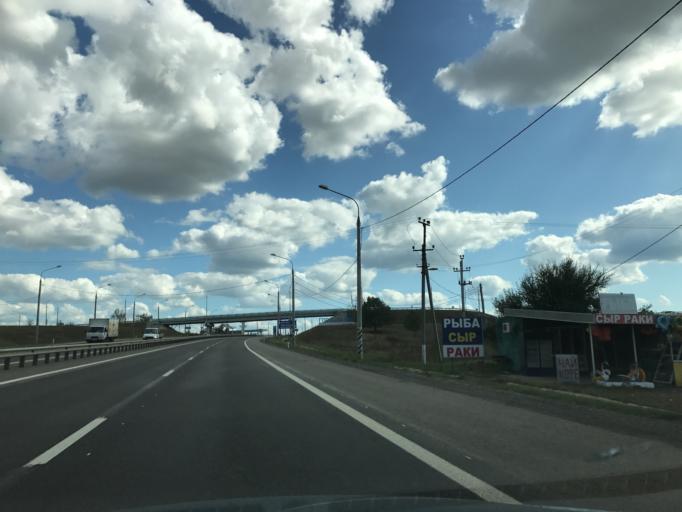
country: RU
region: Adygeya
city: Adygeysk
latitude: 44.8293
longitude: 39.2221
